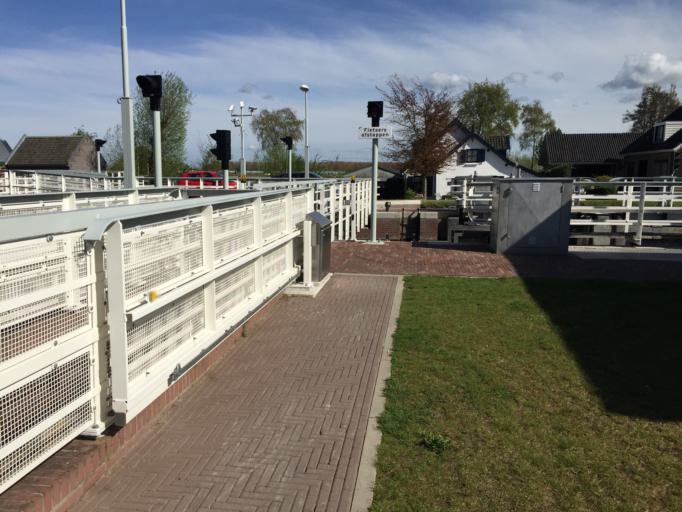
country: NL
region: North Holland
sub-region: Gemeente Aalsmeer
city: Aalsmeer
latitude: 52.2070
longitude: 4.7348
